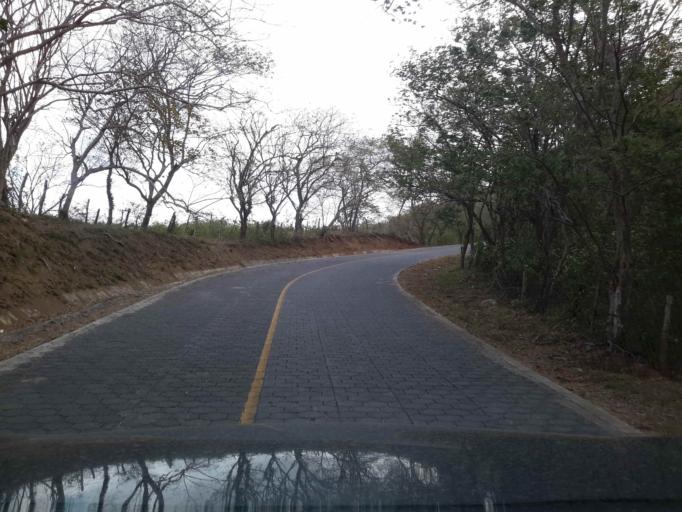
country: NI
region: Rivas
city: San Juan del Sur
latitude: 11.2370
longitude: -85.8322
